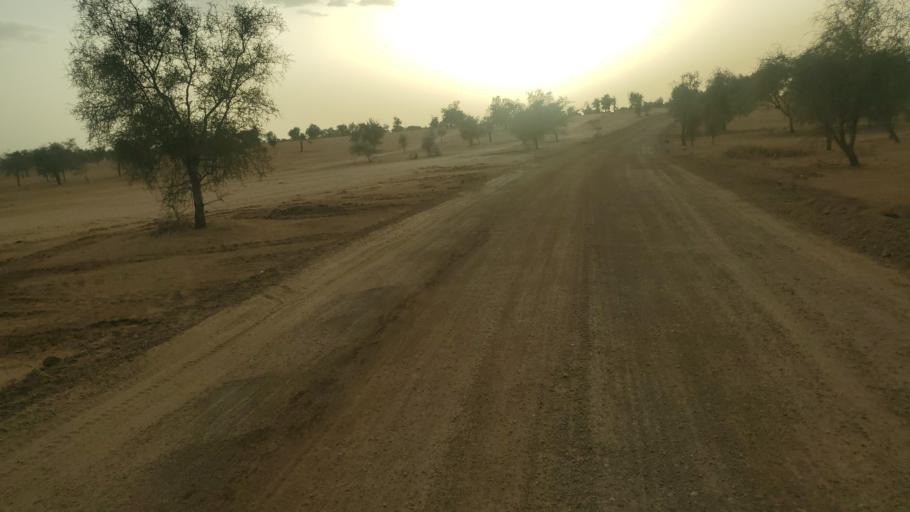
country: SN
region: Louga
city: Dara
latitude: 15.3756
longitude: -15.5899
